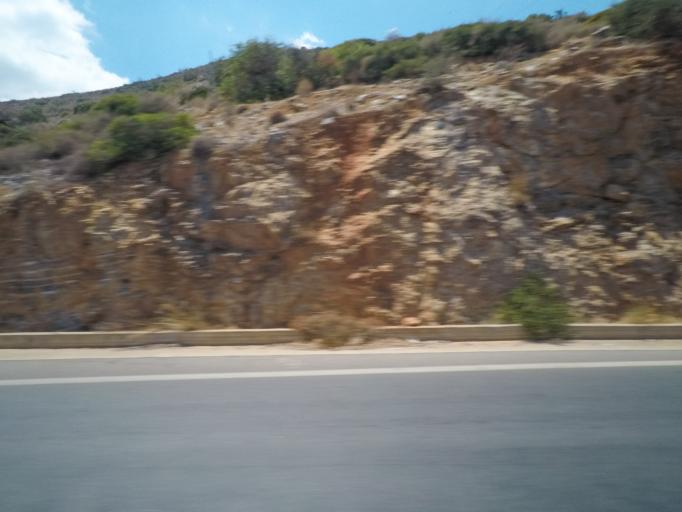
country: GR
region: Crete
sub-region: Nomos Lasithiou
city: Skhisma
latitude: 35.2382
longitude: 25.7272
